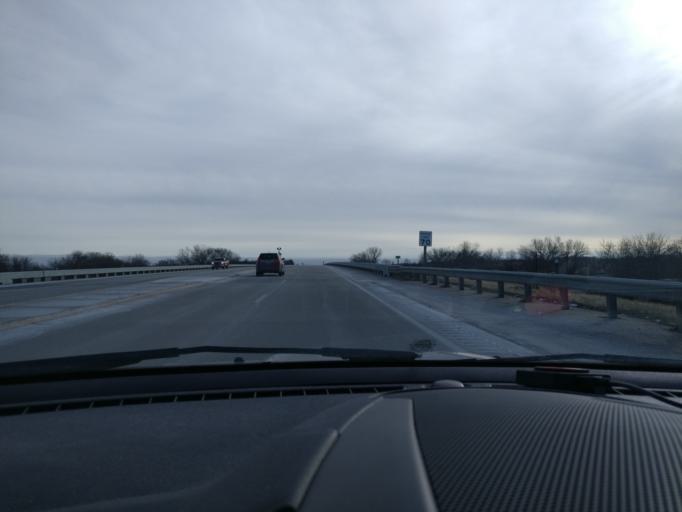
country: US
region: Nebraska
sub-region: Saunders County
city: Wahoo
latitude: 41.2054
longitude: -96.6360
